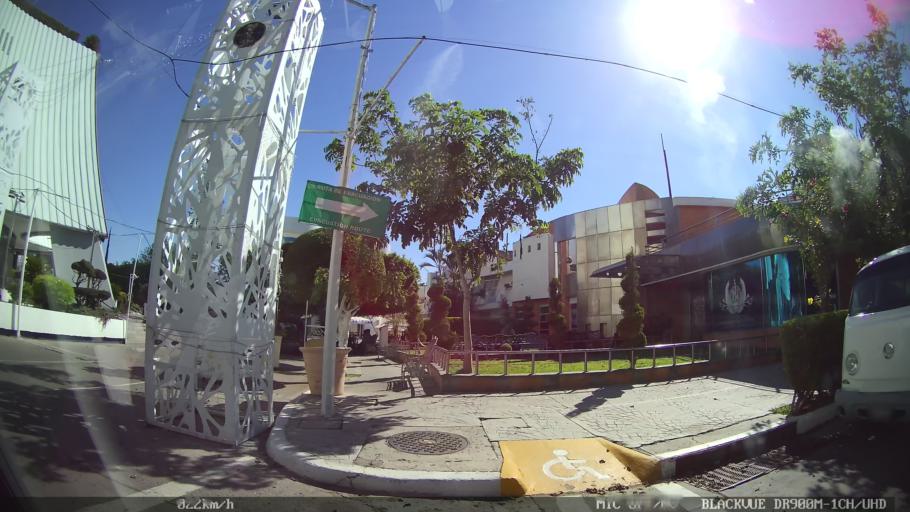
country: MX
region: Jalisco
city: Tlaquepaque
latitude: 20.6727
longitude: -103.2848
